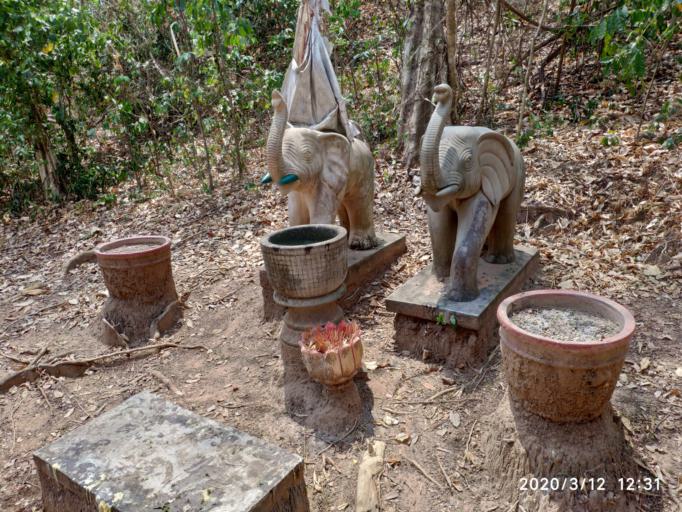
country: KH
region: Preah Vihear
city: Tbeng Meanchey
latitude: 13.7831
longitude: 104.5368
